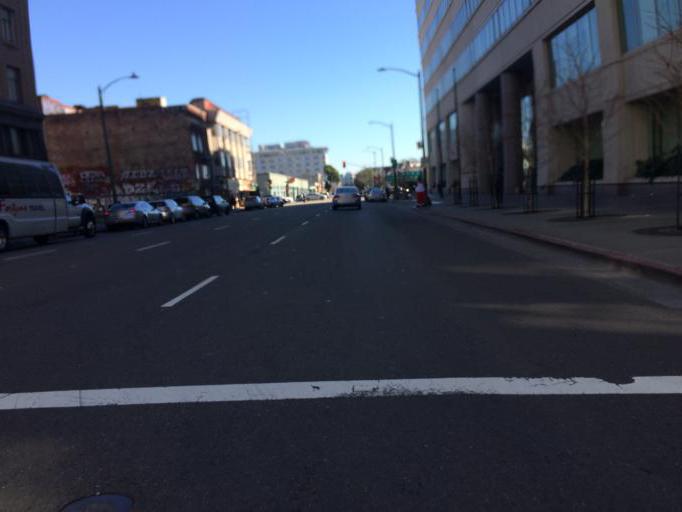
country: US
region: California
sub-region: Alameda County
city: Oakland
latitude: 37.8016
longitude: -122.2712
